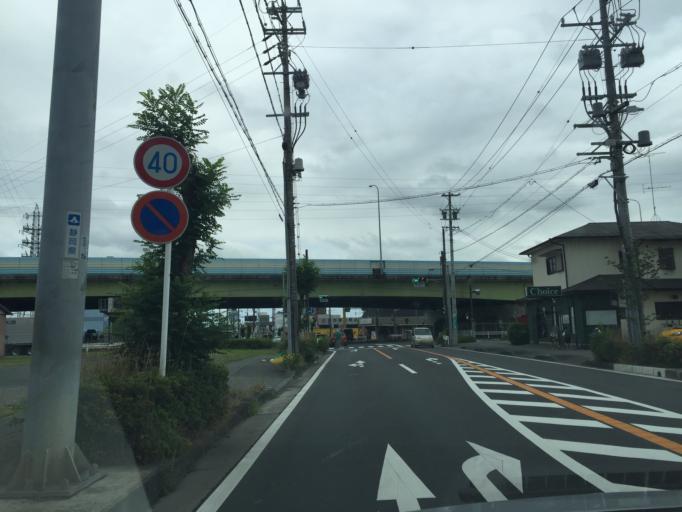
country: JP
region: Shizuoka
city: Fukuroi
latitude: 34.7570
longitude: 137.9185
